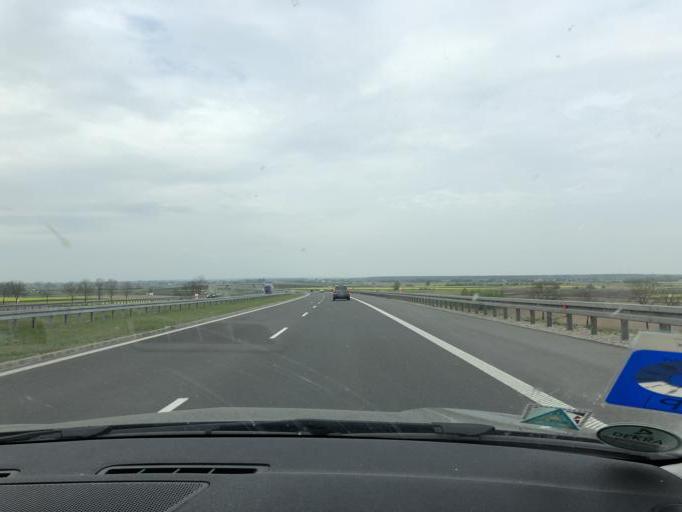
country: PL
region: Subcarpathian Voivodeship
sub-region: Powiat przeworski
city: Rozborz
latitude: 50.0663
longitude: 22.5617
